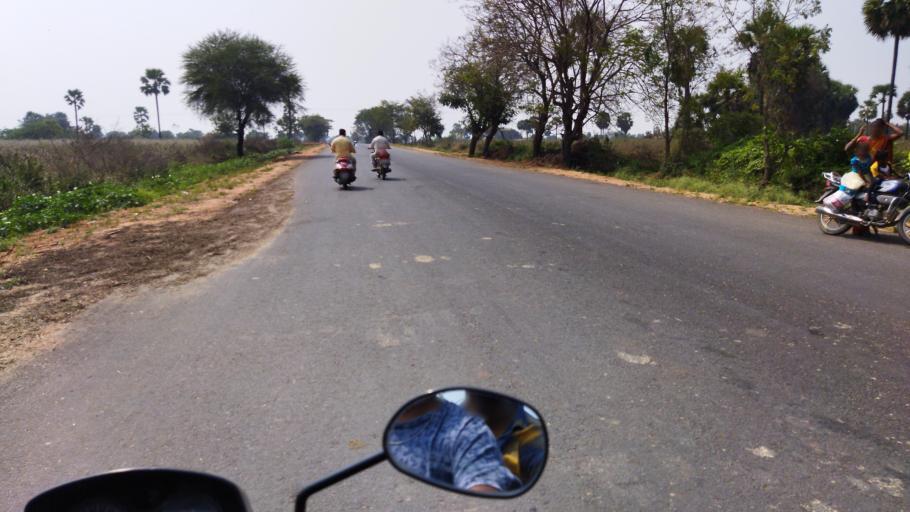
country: IN
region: Telangana
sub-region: Nalgonda
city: Nalgonda
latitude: 17.1577
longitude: 79.4157
